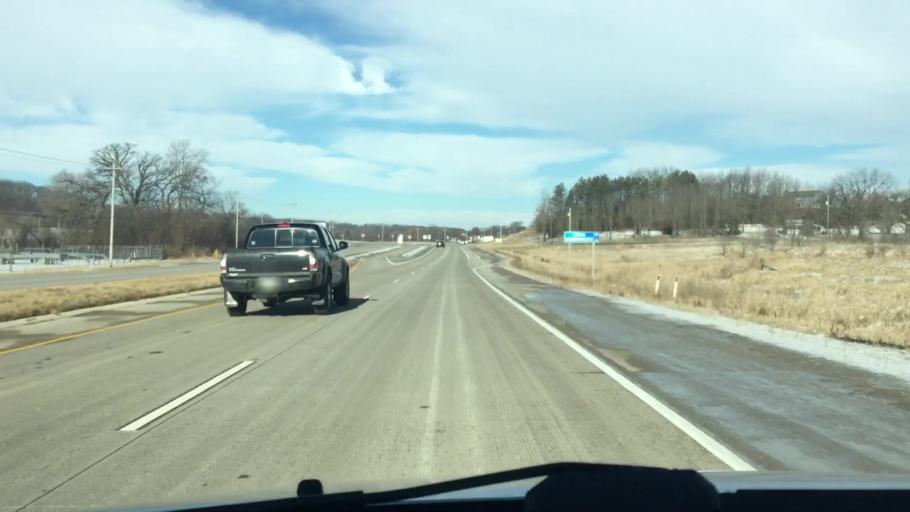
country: US
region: Wisconsin
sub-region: Waukesha County
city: Mukwonago
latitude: 42.8984
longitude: -88.3442
